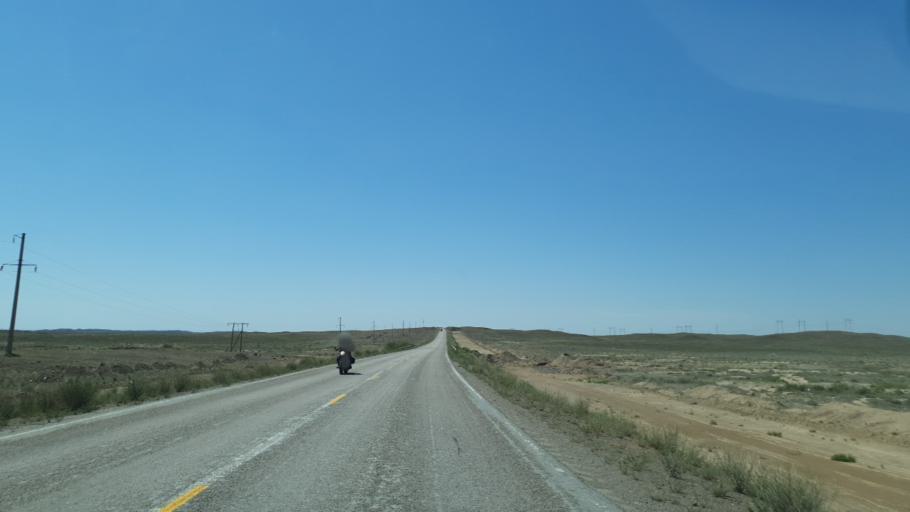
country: KZ
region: Zhambyl
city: Mynaral
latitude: 45.7183
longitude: 73.4027
